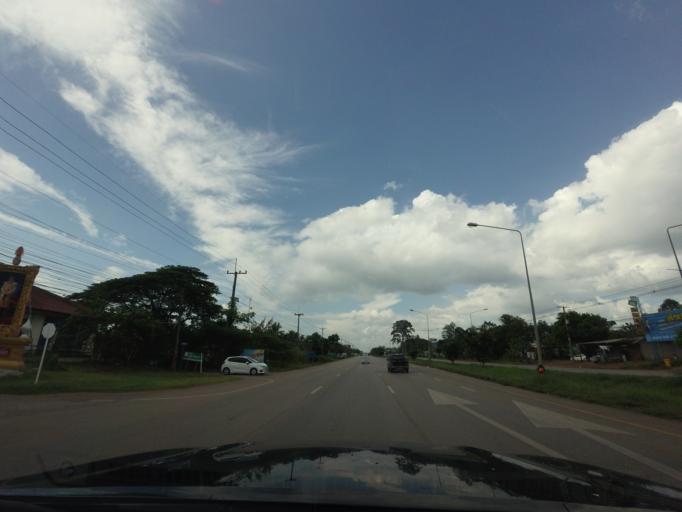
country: TH
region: Changwat Udon Thani
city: Udon Thani
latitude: 17.5439
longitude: 102.8004
